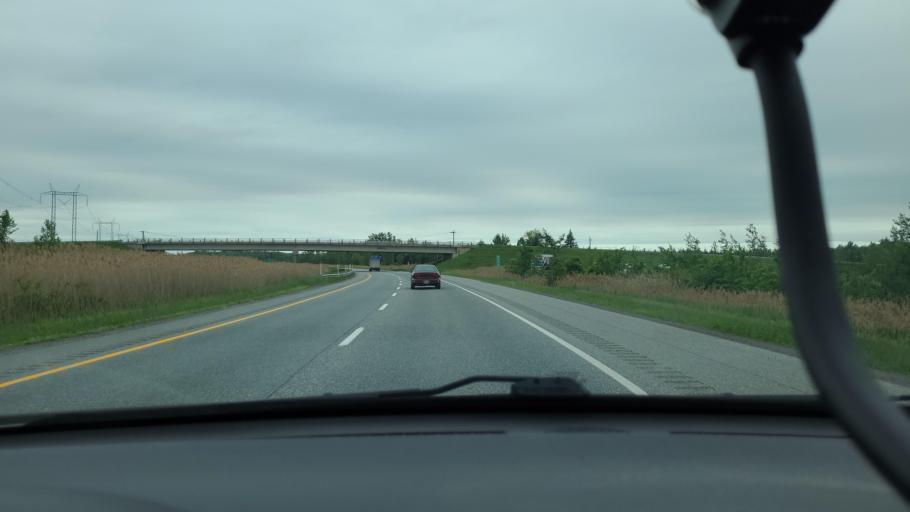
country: CA
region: Quebec
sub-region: Lanaudiere
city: Mascouche
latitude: 45.7783
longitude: -73.5729
